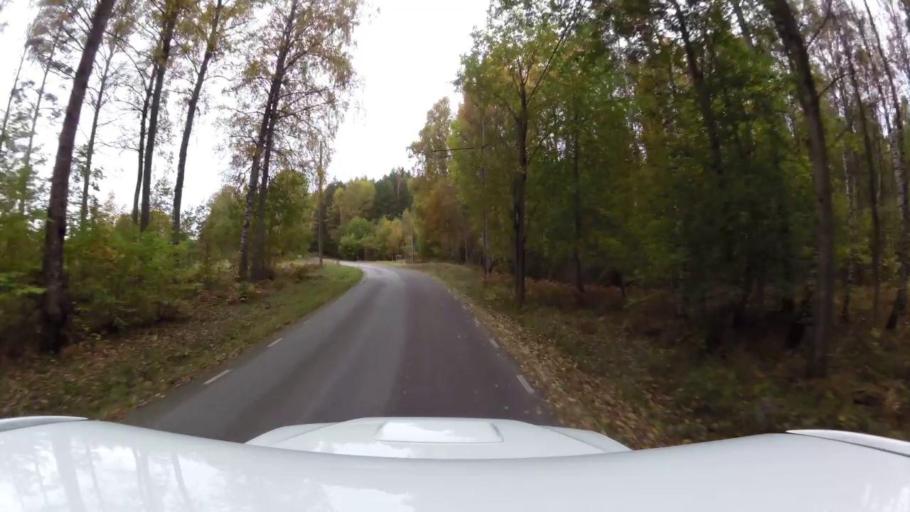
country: SE
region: OEstergoetland
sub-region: Linkopings Kommun
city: Ljungsbro
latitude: 58.5549
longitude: 15.4084
